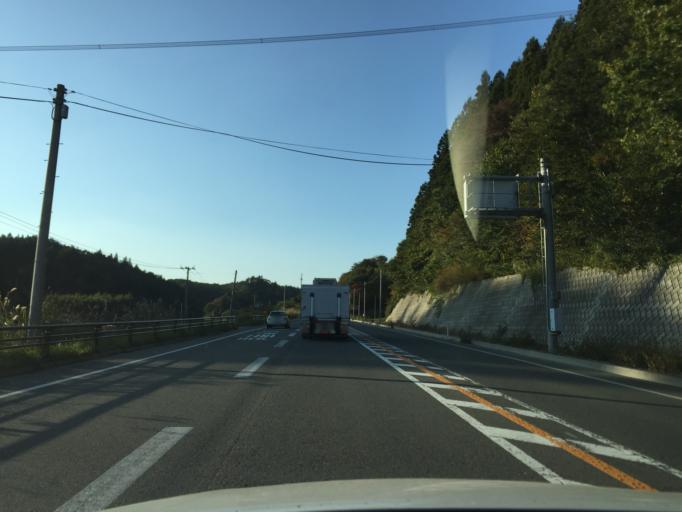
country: JP
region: Fukushima
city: Ishikawa
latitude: 37.1946
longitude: 140.6189
